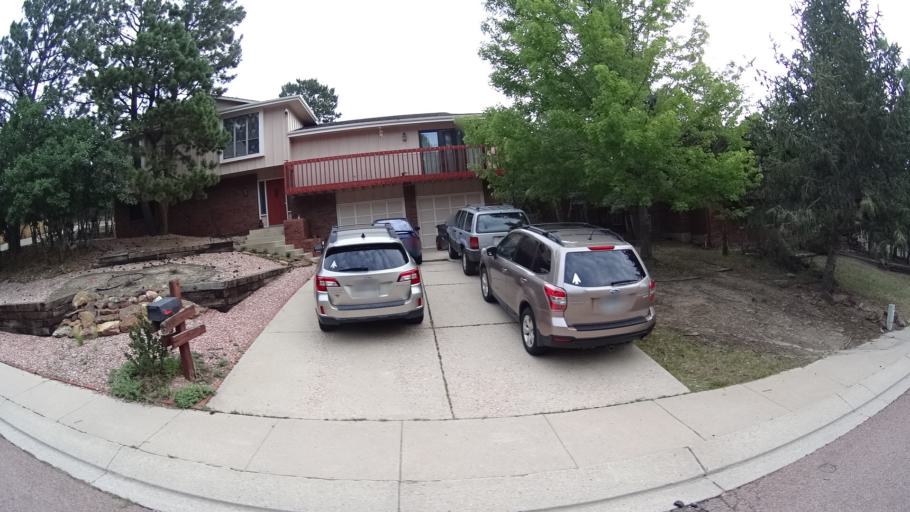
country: US
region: Colorado
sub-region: El Paso County
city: Air Force Academy
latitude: 38.9323
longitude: -104.8399
